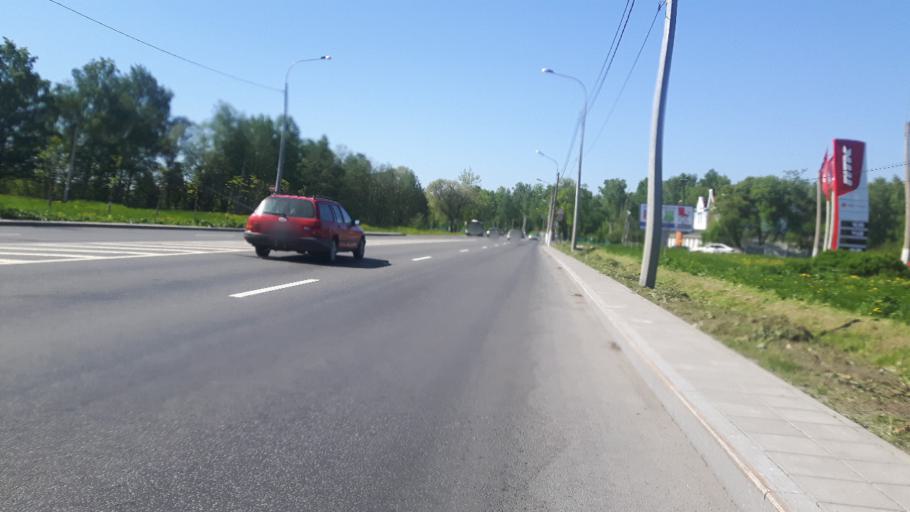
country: RU
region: Leningrad
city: Gorbunki
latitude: 59.8699
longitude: 29.9722
